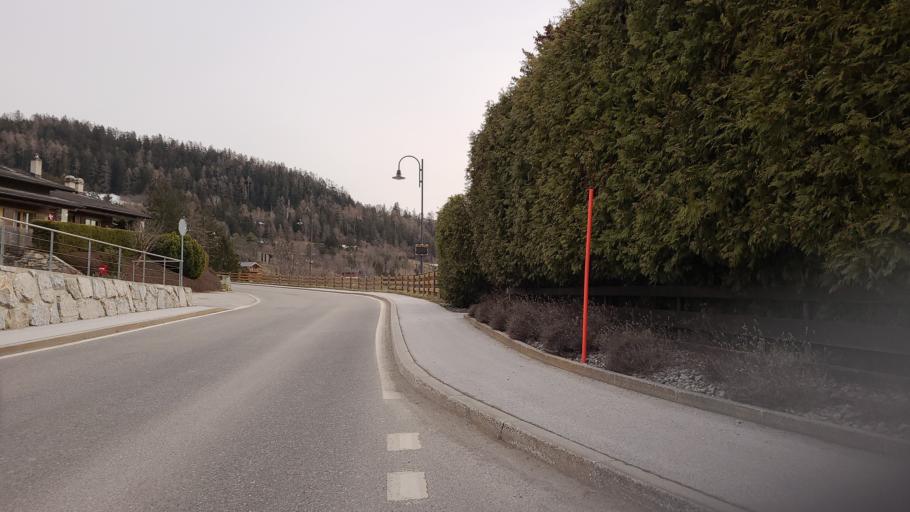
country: CH
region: Valais
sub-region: Sierre District
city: Lens
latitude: 46.2905
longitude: 7.4357
